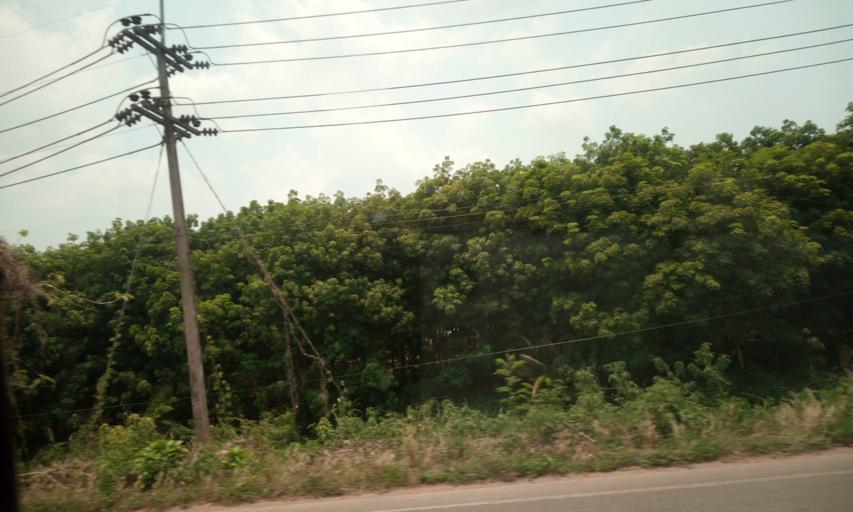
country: TH
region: Phayao
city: Phu Sang
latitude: 19.6135
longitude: 100.2921
